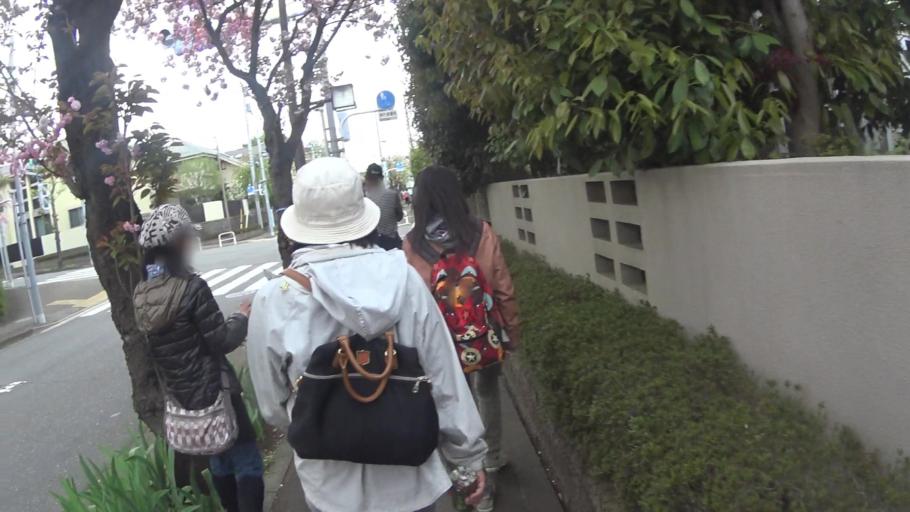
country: JP
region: Tokyo
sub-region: Machida-shi
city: Machida
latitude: 35.5739
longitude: 139.4885
